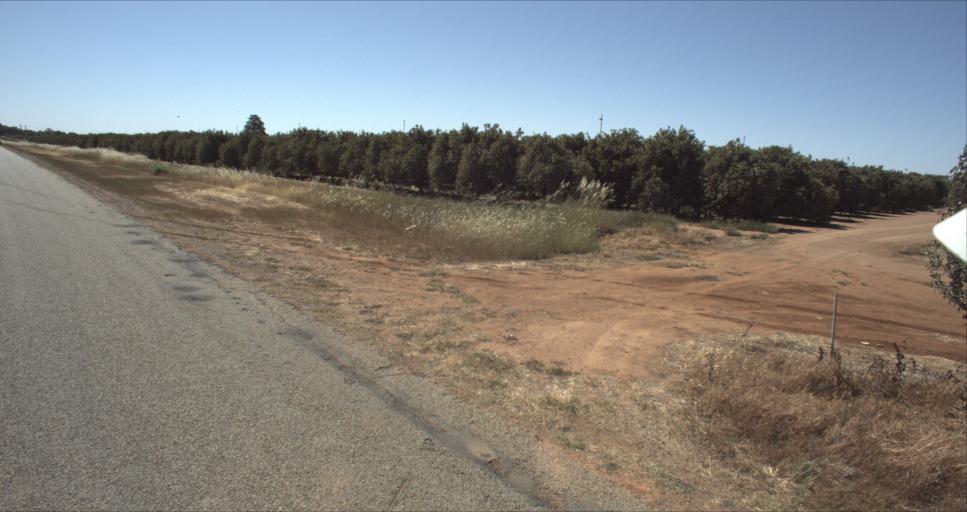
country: AU
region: New South Wales
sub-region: Leeton
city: Leeton
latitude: -34.5448
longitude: 146.3672
